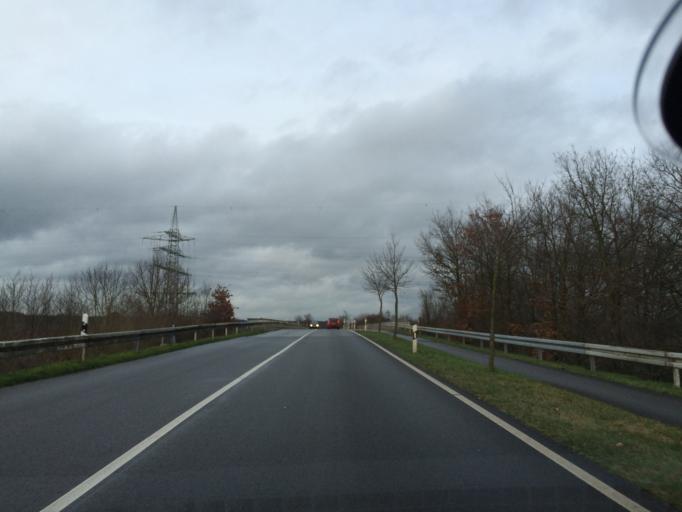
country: DE
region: North Rhine-Westphalia
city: Marl
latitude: 51.7068
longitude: 7.1281
